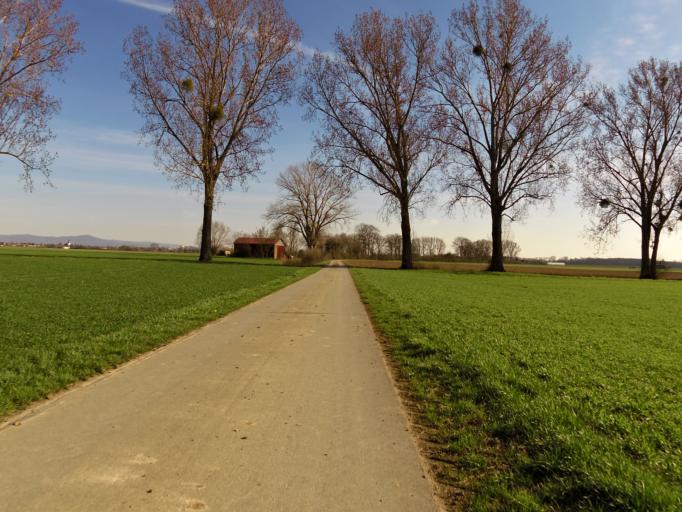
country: DE
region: Hesse
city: Biebesheim
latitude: 49.7893
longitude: 8.4347
